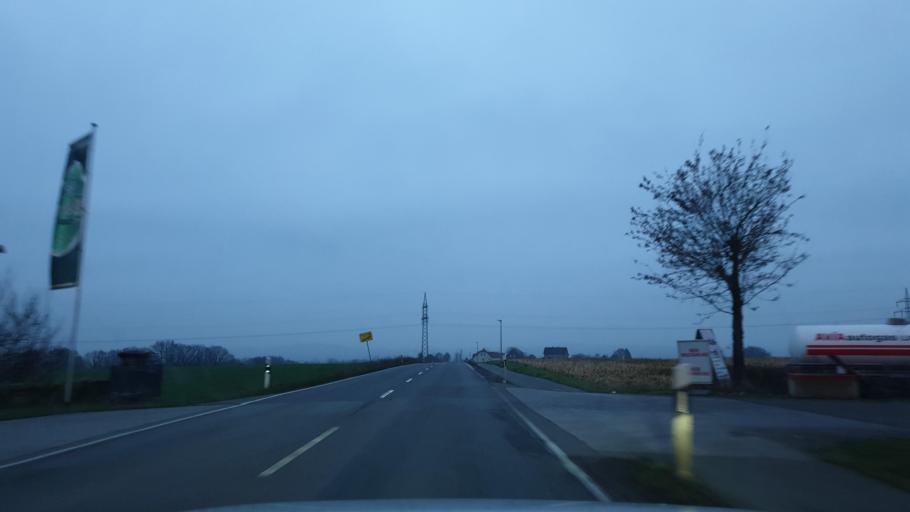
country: DE
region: North Rhine-Westphalia
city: Bad Oeynhausen
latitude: 52.2467
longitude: 8.7839
